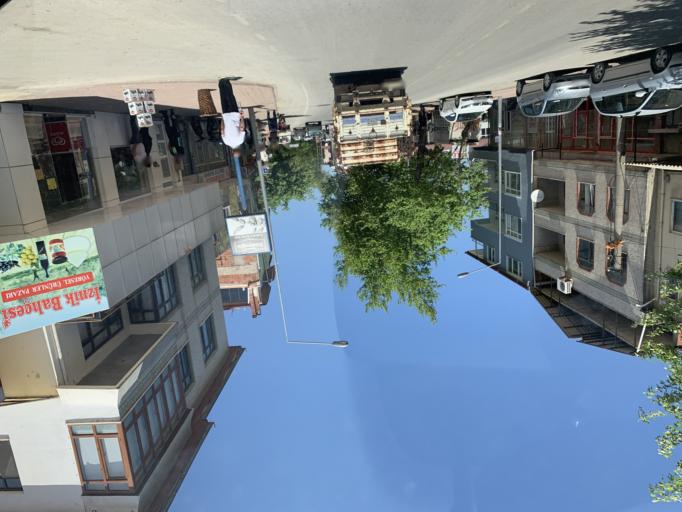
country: TR
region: Bursa
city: Iznik
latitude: 40.4245
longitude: 29.7194
